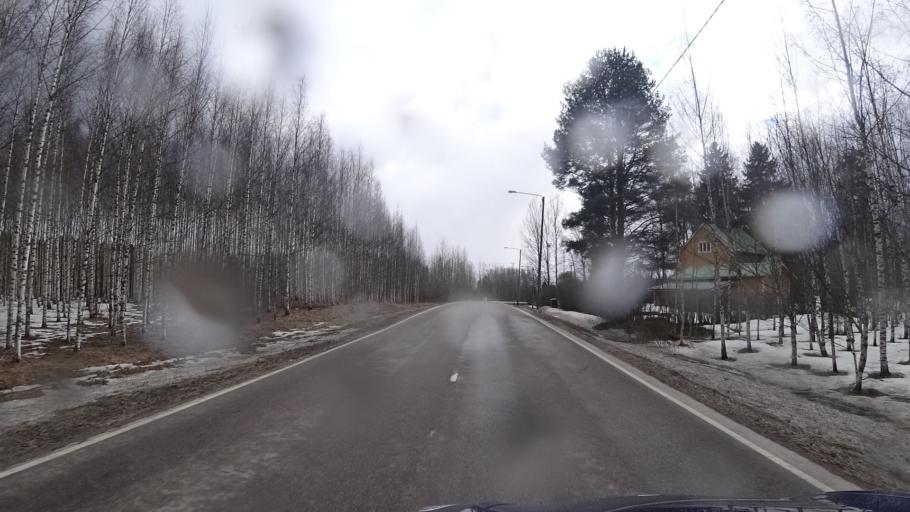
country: FI
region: Kymenlaakso
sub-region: Kotka-Hamina
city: Karhula
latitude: 60.5457
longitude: 26.9125
